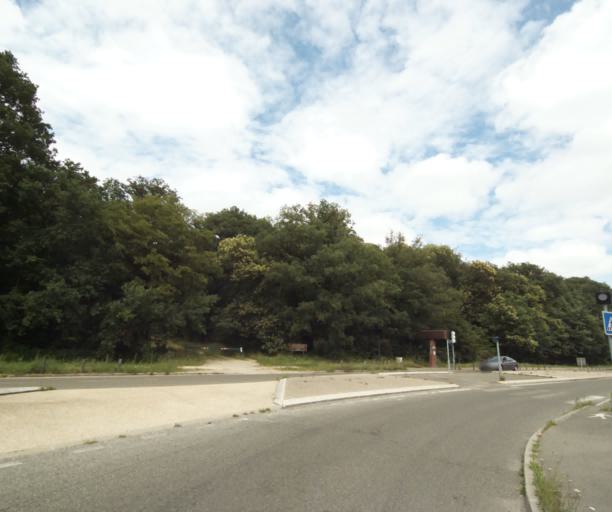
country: FR
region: Ile-de-France
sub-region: Departement des Yvelines
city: Fontenay-le-Fleury
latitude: 48.7982
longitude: 2.0499
